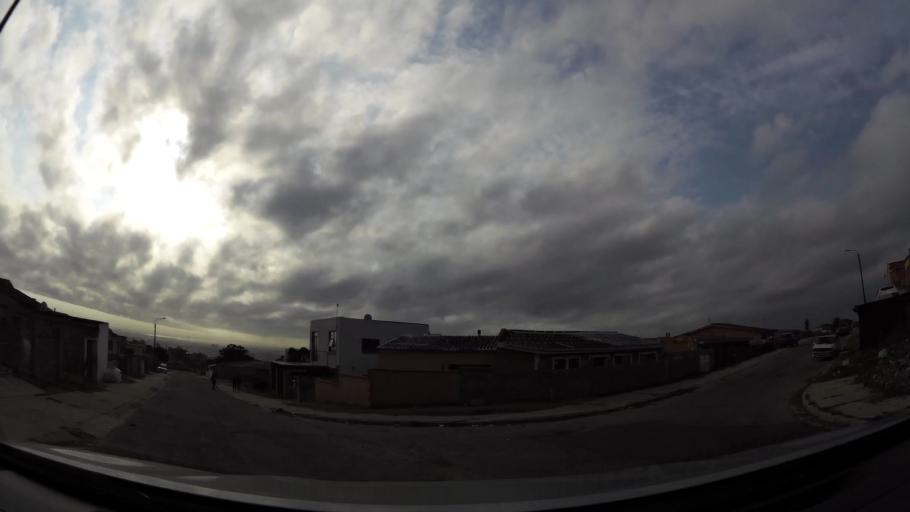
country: ZA
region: Eastern Cape
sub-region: Nelson Mandela Bay Metropolitan Municipality
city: Port Elizabeth
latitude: -33.9157
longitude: 25.5439
